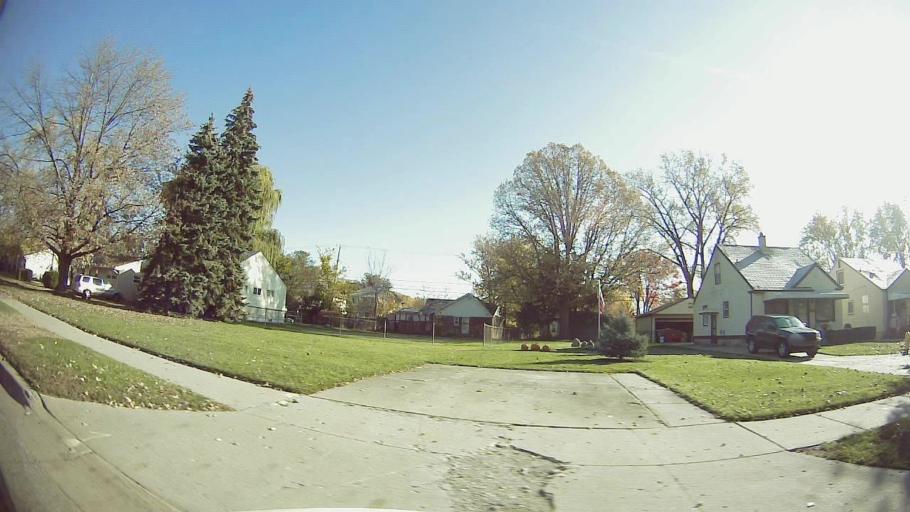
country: US
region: Michigan
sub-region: Oakland County
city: Berkley
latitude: 42.5005
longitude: -83.2029
